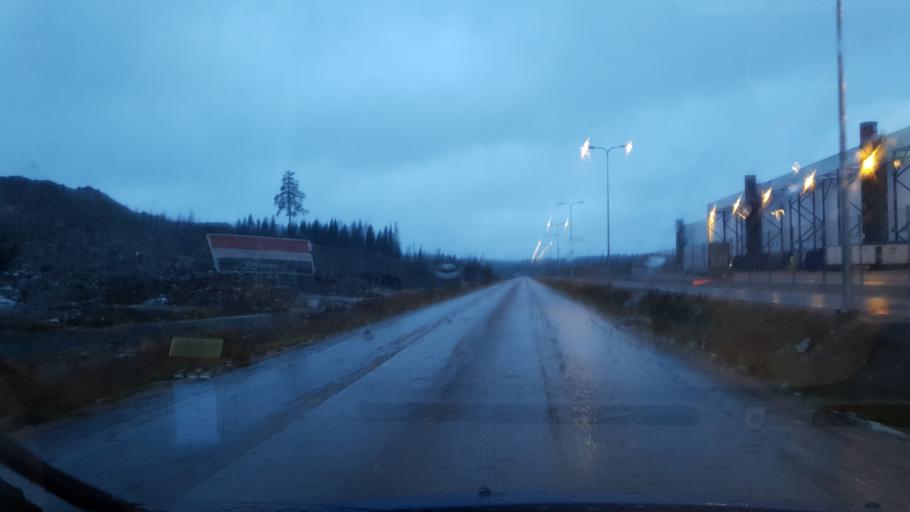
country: FI
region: Uusimaa
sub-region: Helsinki
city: Kerava
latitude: 60.3744
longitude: 25.1627
